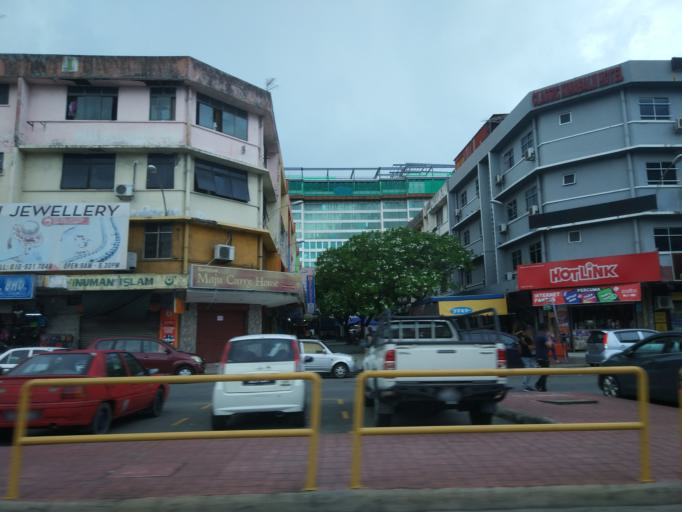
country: MY
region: Sabah
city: Kota Kinabalu
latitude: 5.9794
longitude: 116.0732
